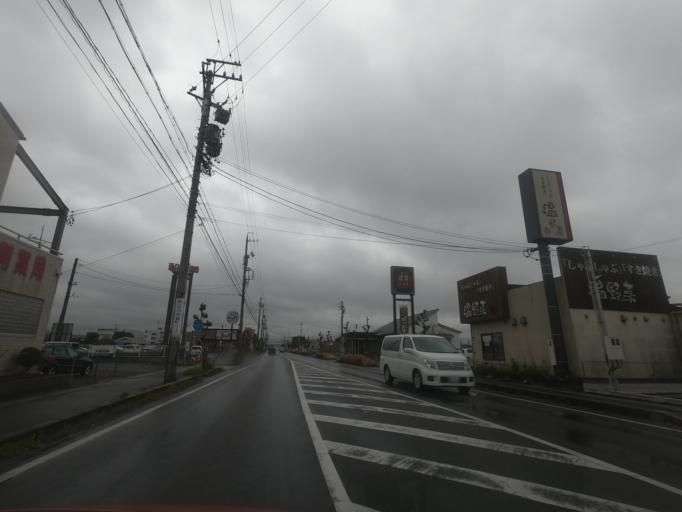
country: JP
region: Aichi
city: Kasugai
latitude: 35.2704
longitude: 136.9727
